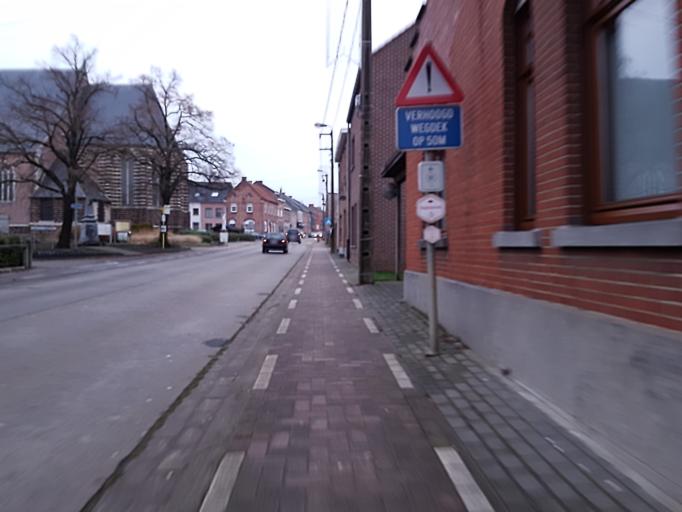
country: BE
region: Flanders
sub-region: Provincie Vlaams-Brabant
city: Begijnendijk
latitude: 50.9842
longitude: 4.7818
